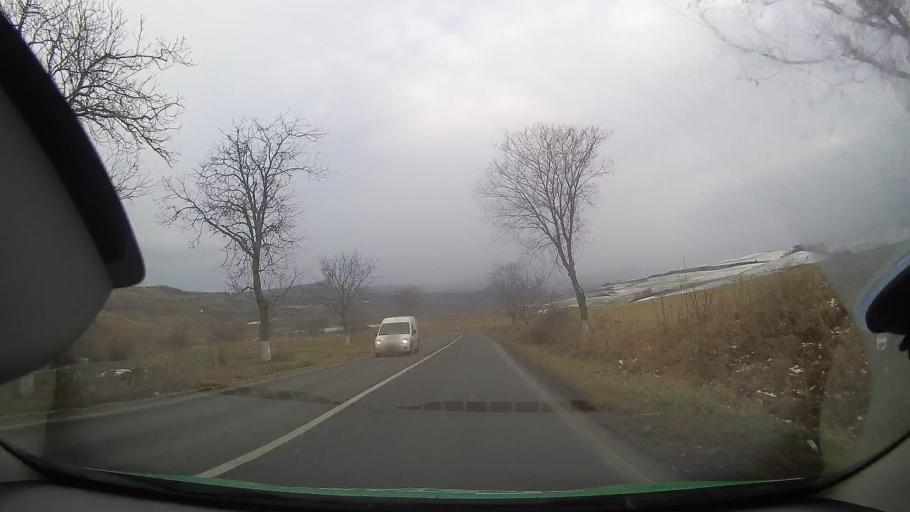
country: RO
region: Sibiu
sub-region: Comuna Blajel
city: Blajel
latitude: 46.2384
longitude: 24.3037
